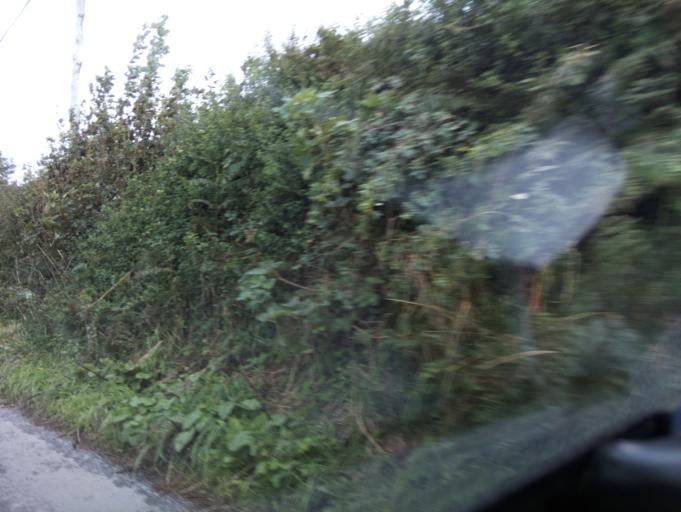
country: GB
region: England
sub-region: Devon
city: Dartmouth
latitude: 50.3319
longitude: -3.5843
